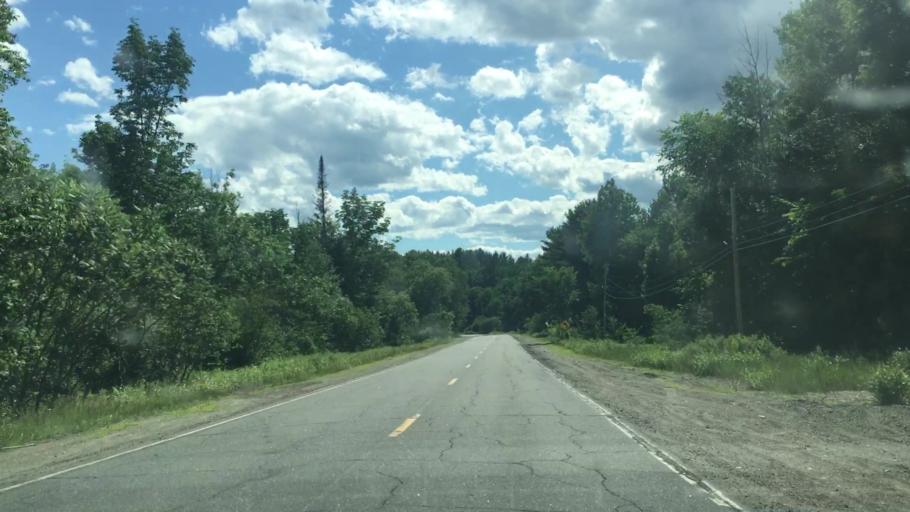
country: US
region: Maine
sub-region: Franklin County
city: Farmington
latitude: 44.6849
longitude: -70.1281
